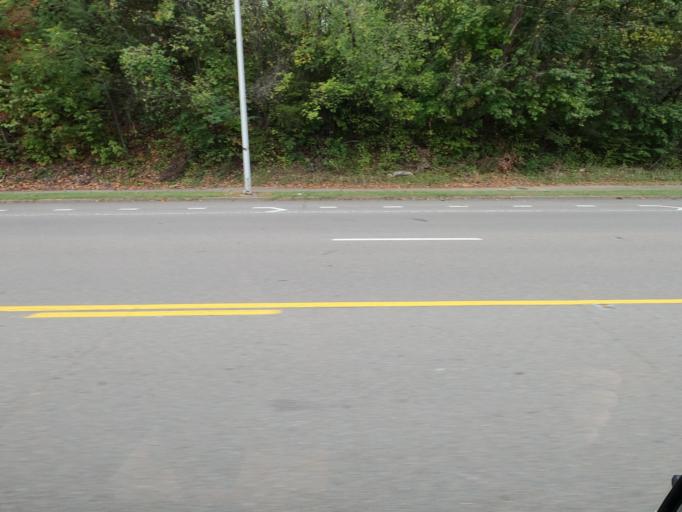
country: US
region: Tennessee
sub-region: Sullivan County
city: Kingsport
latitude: 36.5651
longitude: -82.5651
